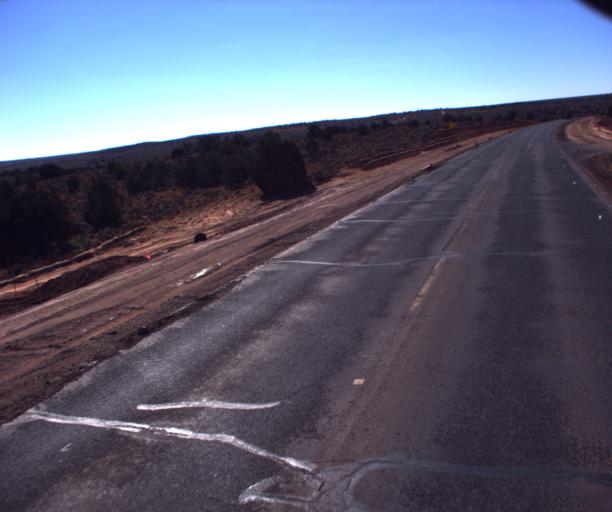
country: US
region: Arizona
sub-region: Apache County
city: Ganado
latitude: 35.7128
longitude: -109.4910
